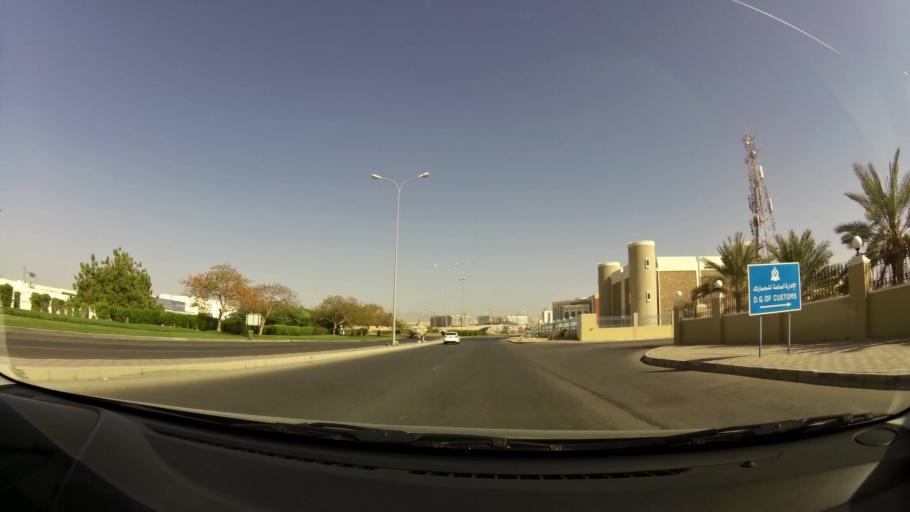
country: OM
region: Muhafazat Masqat
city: Bawshar
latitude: 23.5835
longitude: 58.2915
